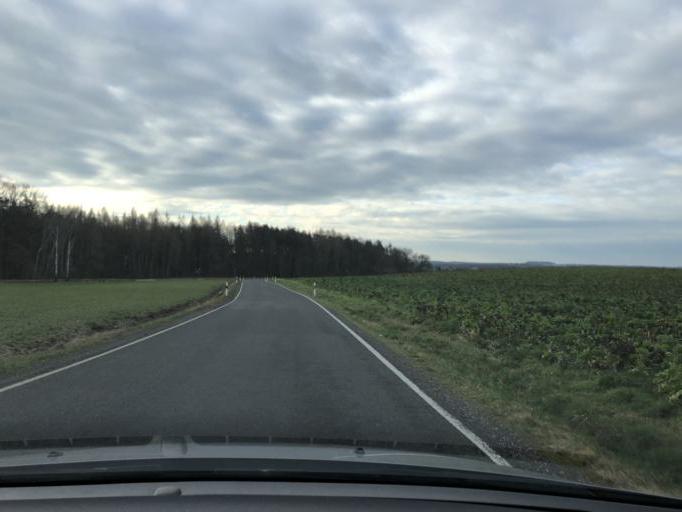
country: DE
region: Saxony
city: Grossbothen
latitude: 51.2004
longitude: 12.7895
